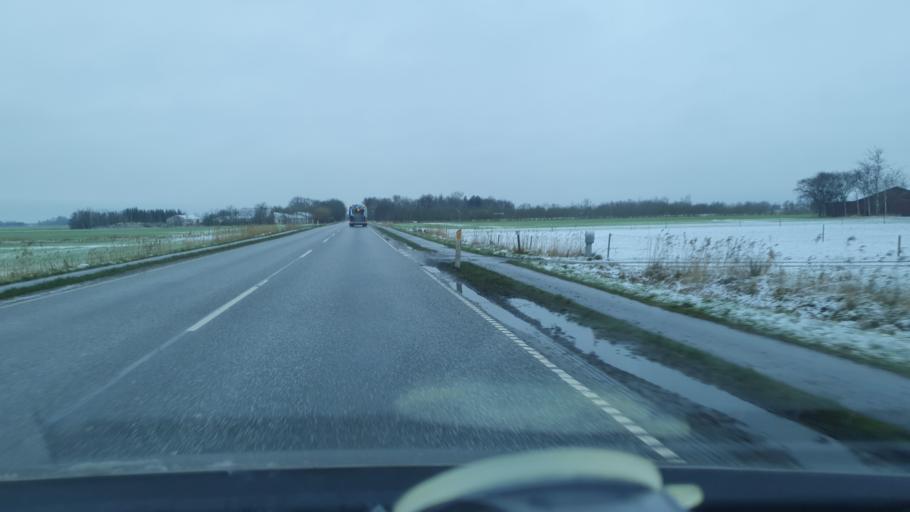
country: DK
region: North Denmark
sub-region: Jammerbugt Kommune
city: Brovst
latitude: 57.1190
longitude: 9.6140
